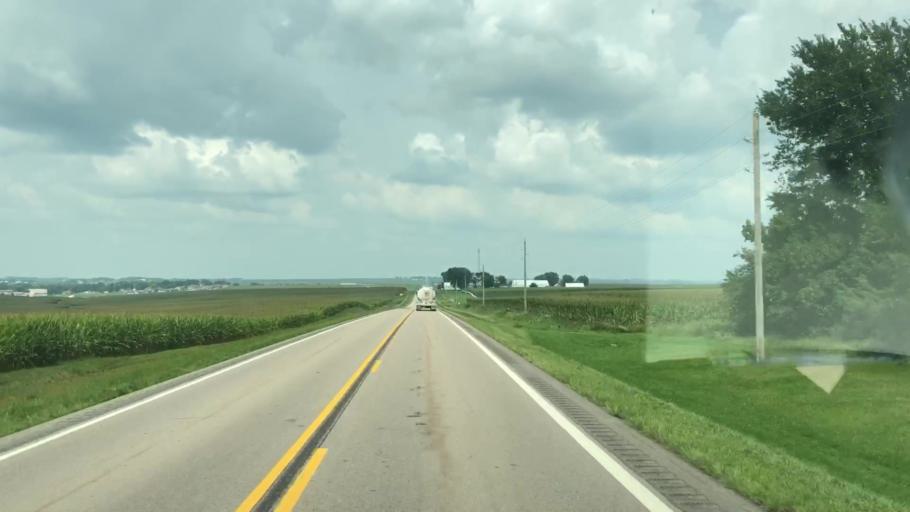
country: US
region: Iowa
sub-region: Plymouth County
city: Remsen
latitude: 42.7981
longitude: -95.9577
